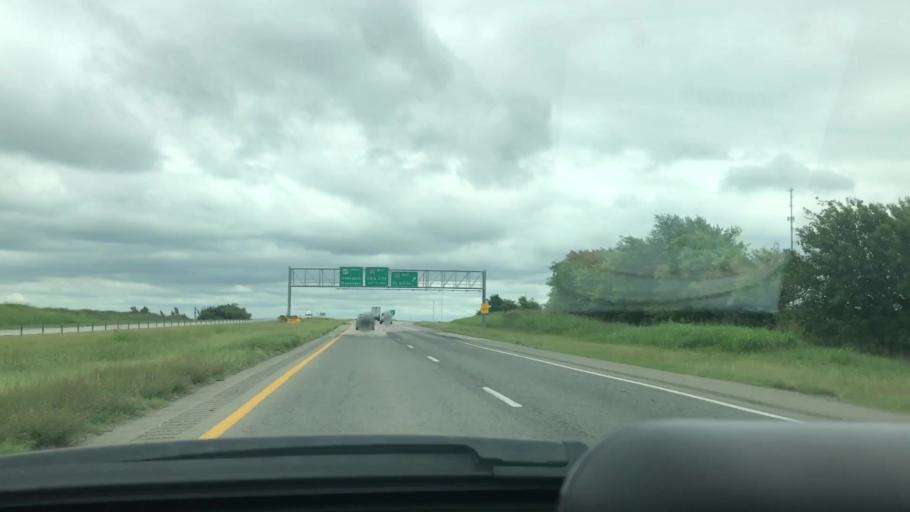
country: US
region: Oklahoma
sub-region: McIntosh County
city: Checotah
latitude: 35.4518
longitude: -95.5470
